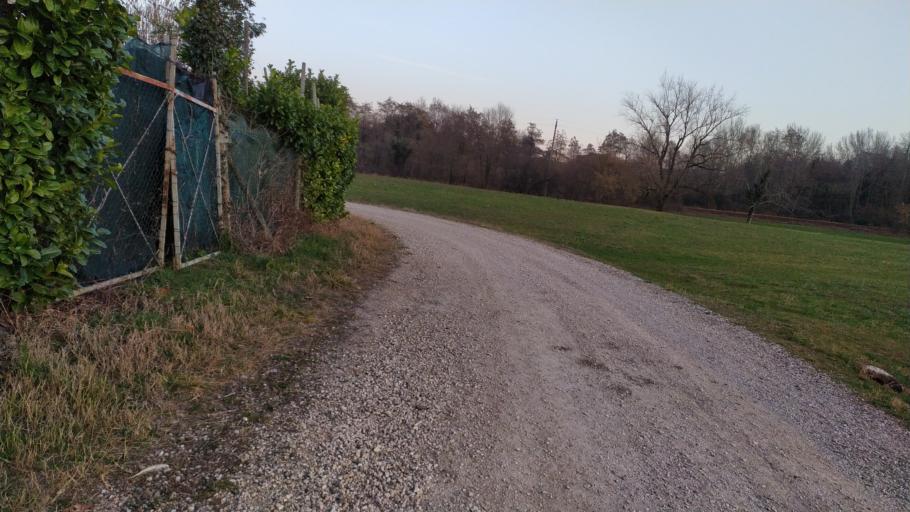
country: IT
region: Veneto
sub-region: Provincia di Vicenza
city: San Vito di Leguzzano
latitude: 45.6838
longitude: 11.3665
